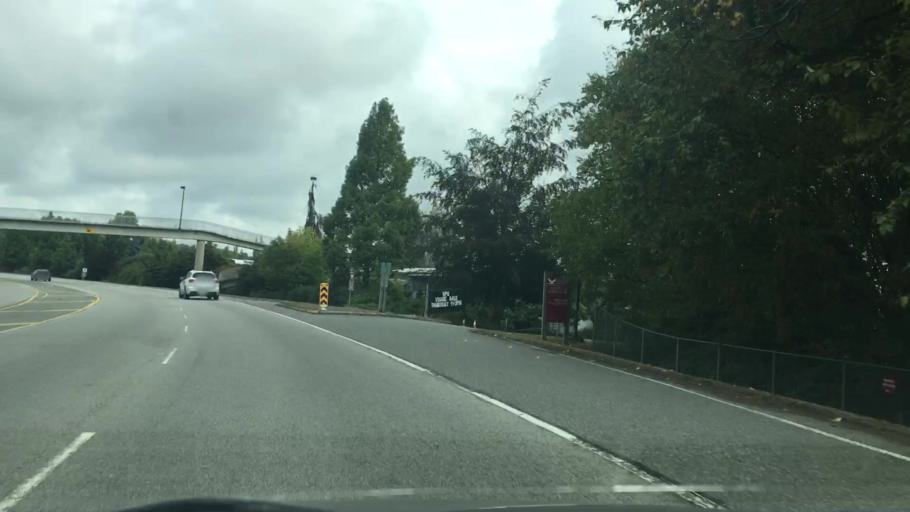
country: CA
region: British Columbia
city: Langley
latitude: 49.1095
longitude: -122.6428
